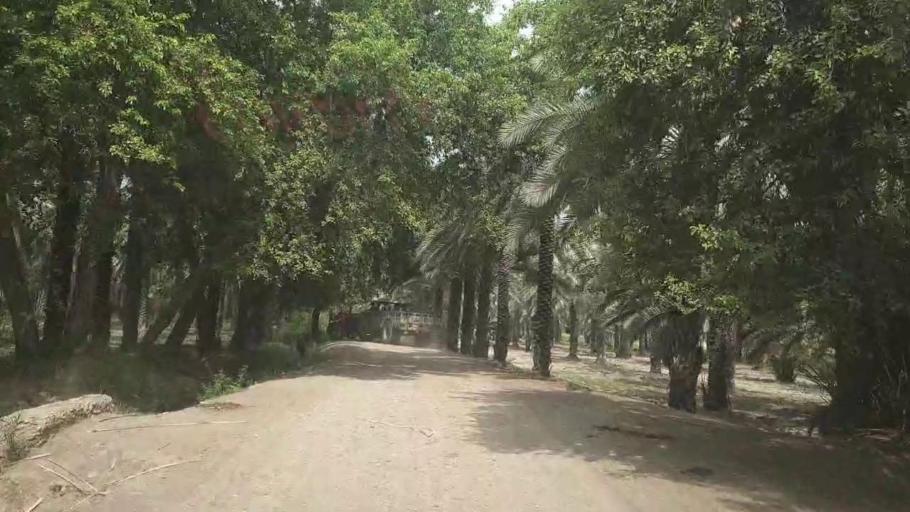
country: PK
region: Sindh
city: Khairpur
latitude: 27.5802
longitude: 68.7424
